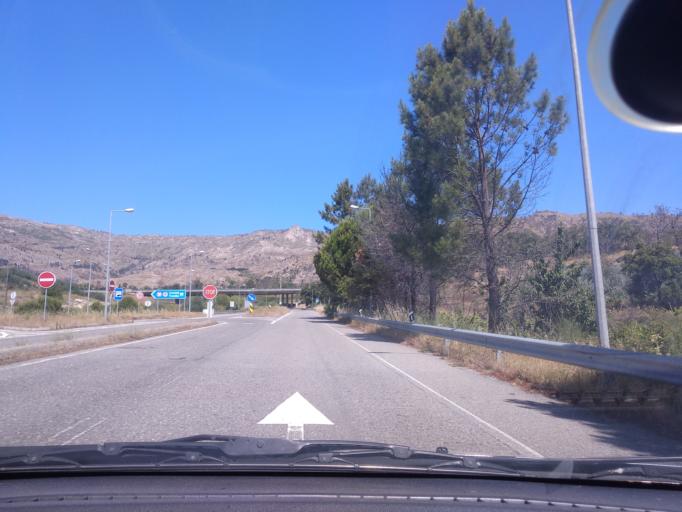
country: PT
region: Castelo Branco
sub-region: Concelho do Fundao
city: Fundao
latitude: 40.0761
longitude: -7.4755
